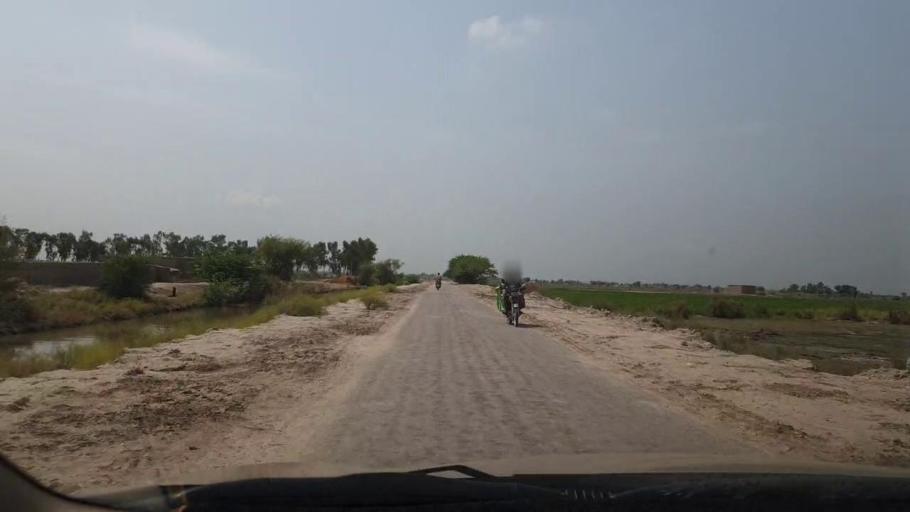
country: PK
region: Sindh
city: Goth Garelo
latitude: 27.5062
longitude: 68.1140
